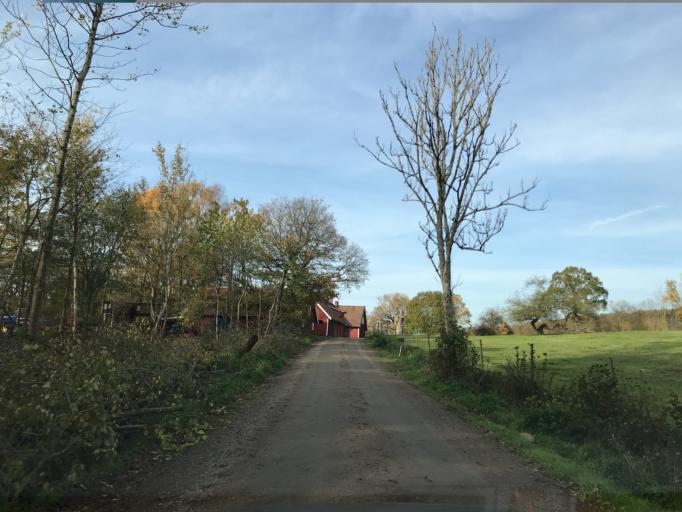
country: SE
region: Skane
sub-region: Bjuvs Kommun
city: Billesholm
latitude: 56.0670
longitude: 13.0196
